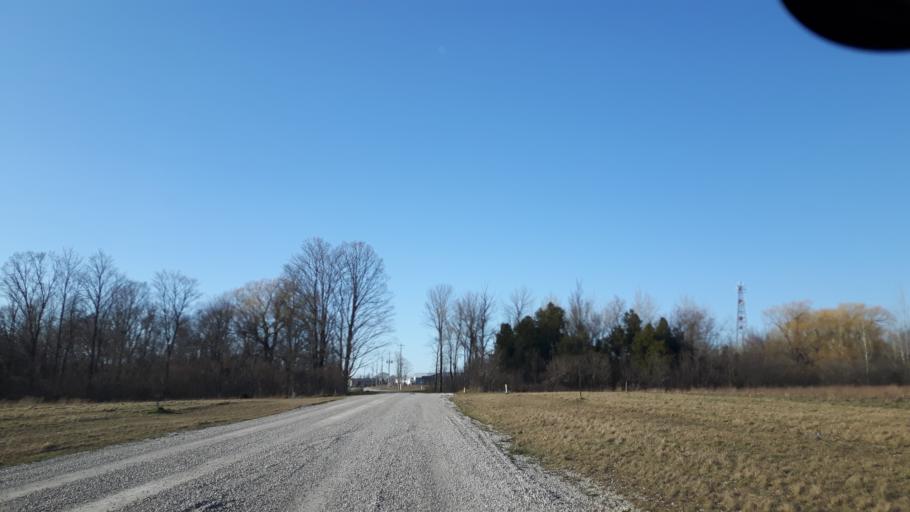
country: CA
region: Ontario
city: Goderich
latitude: 43.7240
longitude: -81.6932
